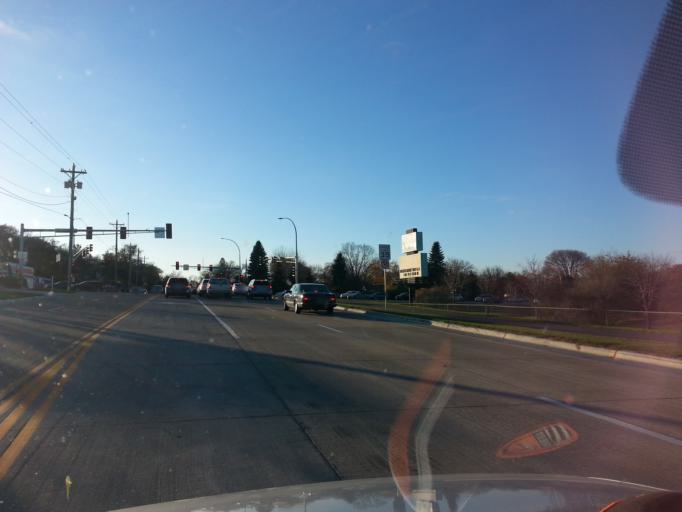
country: US
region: Minnesota
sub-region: Olmsted County
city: Rochester
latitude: 44.0000
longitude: -92.4635
